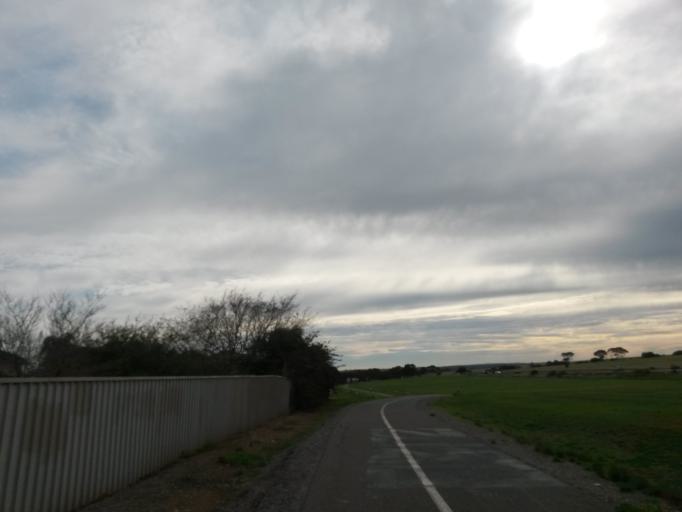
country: AU
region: South Australia
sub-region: Onkaparinga
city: Moana
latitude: -35.2053
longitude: 138.4903
